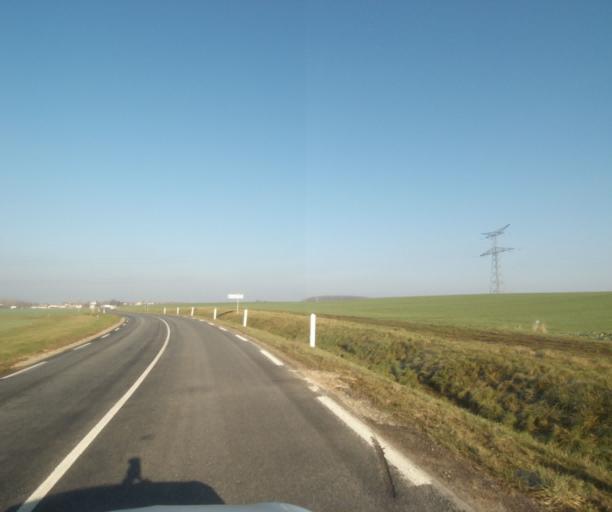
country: FR
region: Champagne-Ardenne
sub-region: Departement de la Haute-Marne
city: Wassy
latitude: 48.5160
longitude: 4.9360
